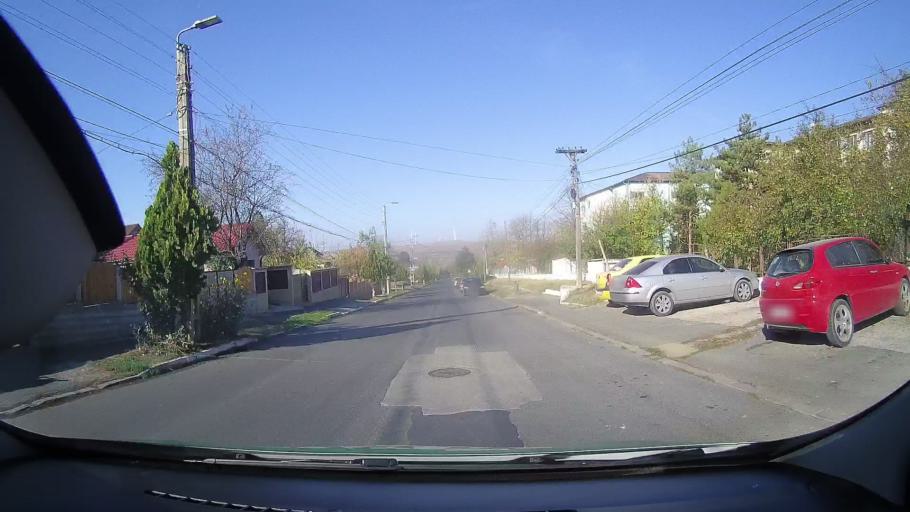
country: RO
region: Tulcea
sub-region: Oras Babadag
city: Babadag
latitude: 44.8875
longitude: 28.7329
